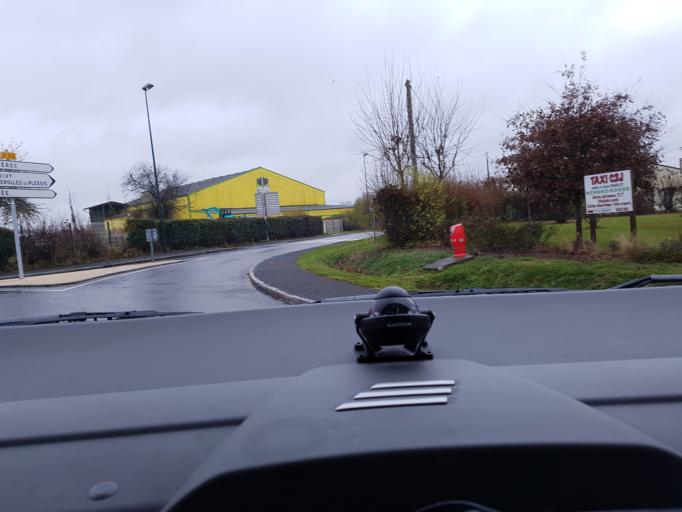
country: FR
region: Pays de la Loire
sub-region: Departement de la Mayenne
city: Gorron
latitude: 48.4157
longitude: -0.8247
